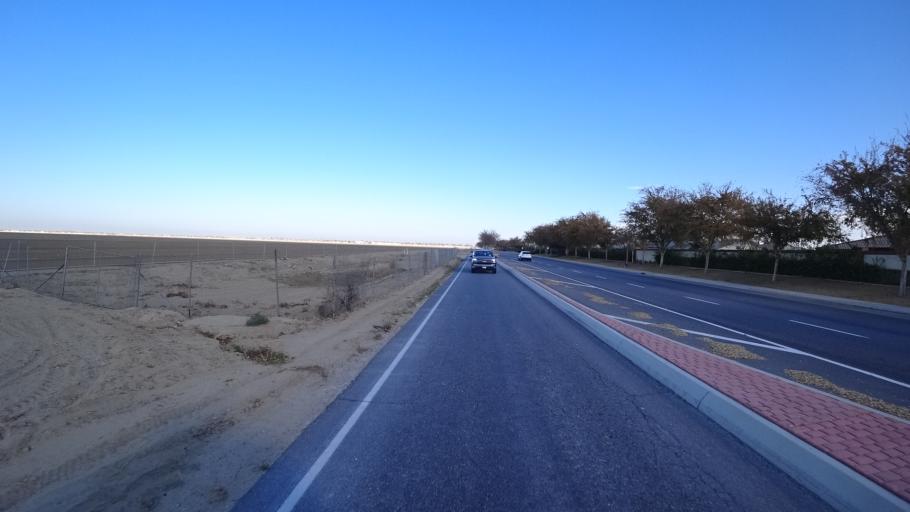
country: US
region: California
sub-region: Kern County
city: Rosedale
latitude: 35.3272
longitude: -119.1458
